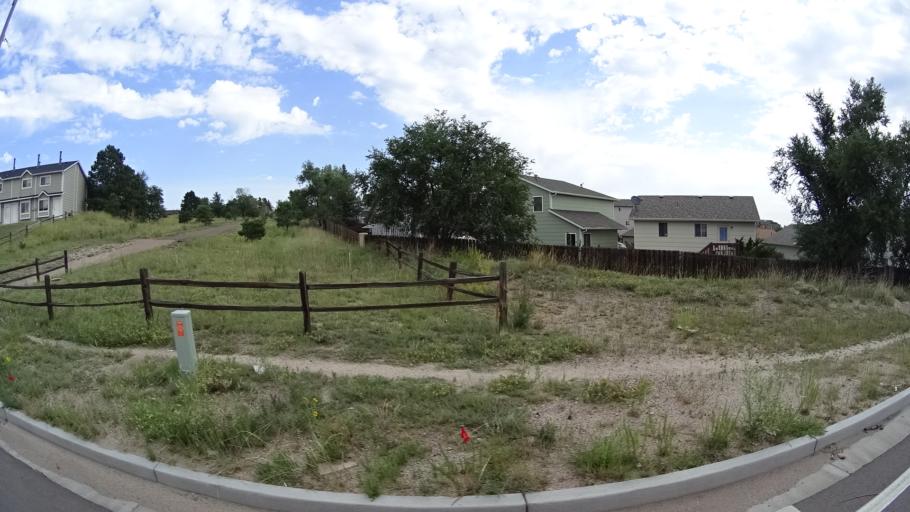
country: US
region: Colorado
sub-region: El Paso County
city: Cimarron Hills
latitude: 38.8953
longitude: -104.7268
